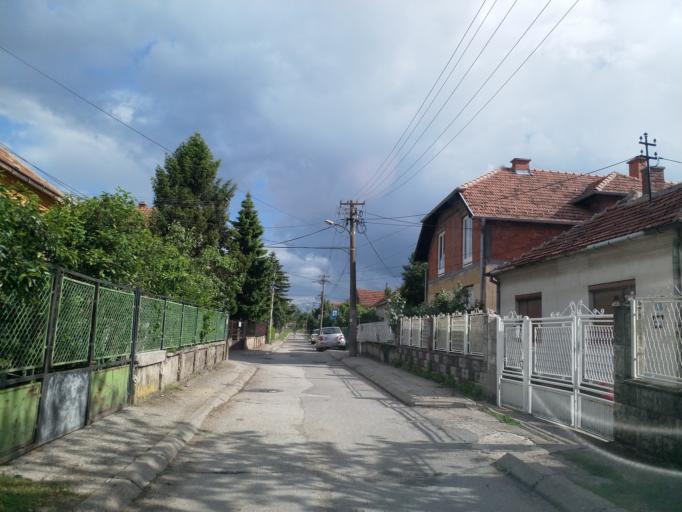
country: RS
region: Central Serbia
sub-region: Pomoravski Okrug
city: Paracin
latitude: 43.8572
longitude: 21.4158
